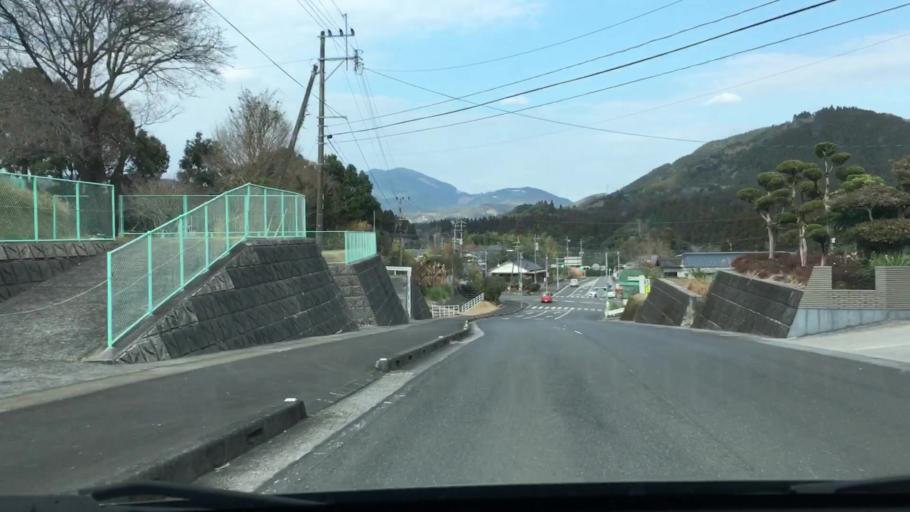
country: JP
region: Miyazaki
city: Kushima
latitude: 31.5252
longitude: 131.2370
